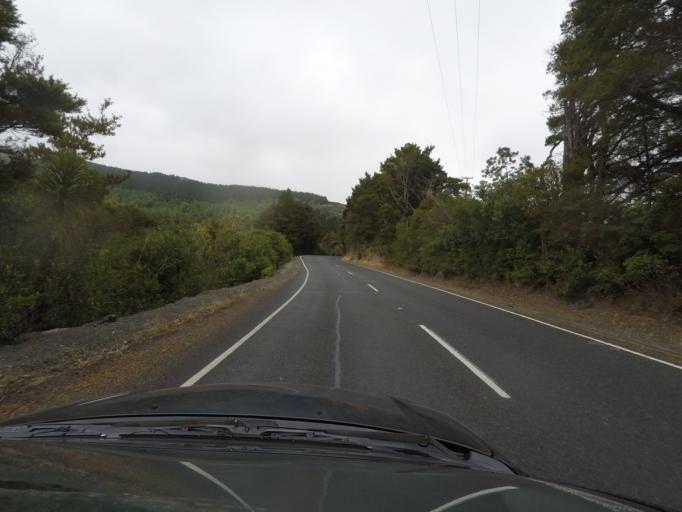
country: NZ
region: Auckland
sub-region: Auckland
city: Warkworth
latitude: -36.2654
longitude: 174.7175
